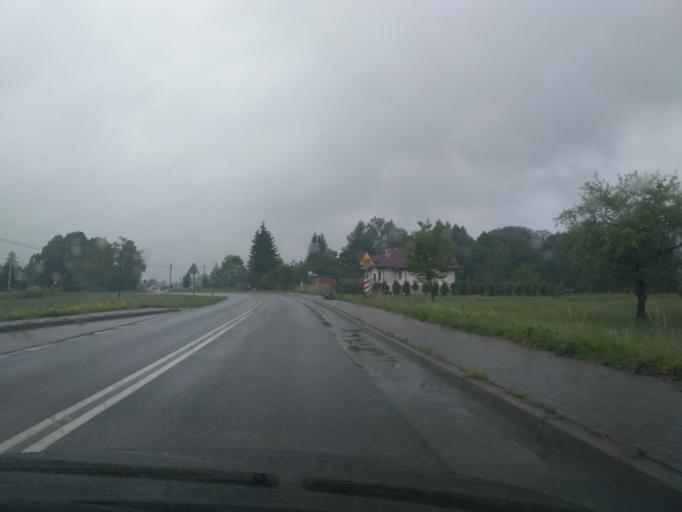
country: PL
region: Subcarpathian Voivodeship
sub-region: Powiat krosnienski
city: Leki
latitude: 49.7935
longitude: 21.6526
